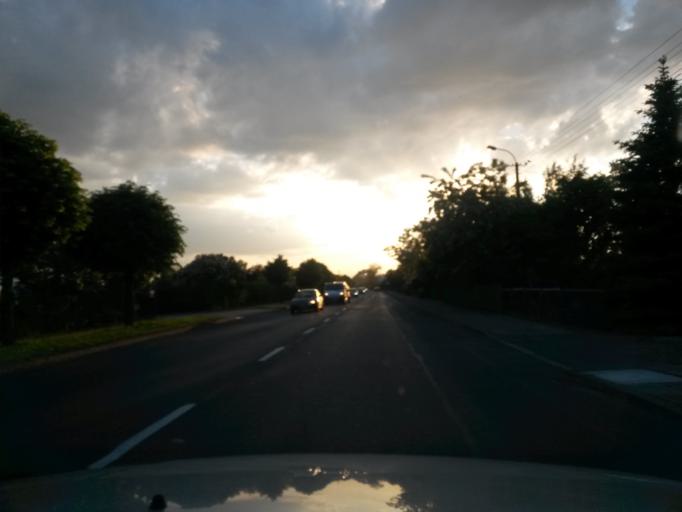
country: PL
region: Lodz Voivodeship
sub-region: Powiat wielunski
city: Mokrsko
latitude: 51.2603
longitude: 18.4809
